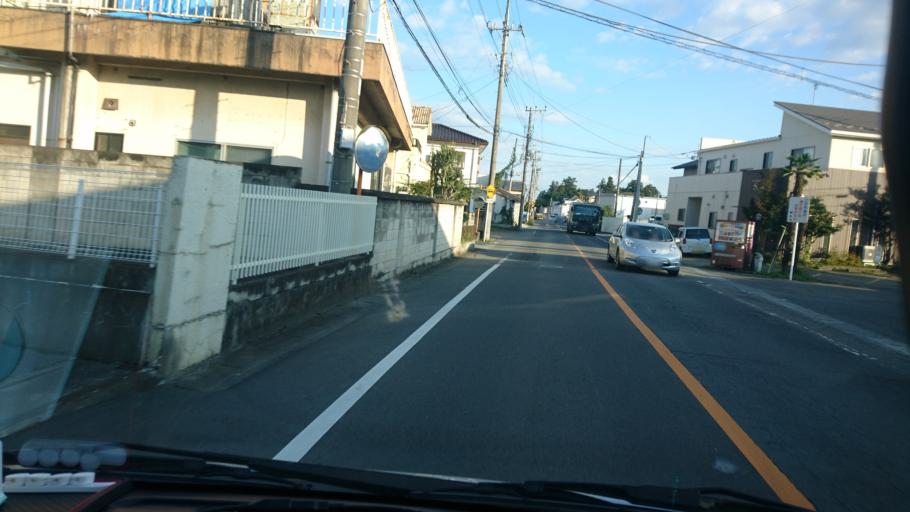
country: JP
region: Gunma
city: Omamacho-omama
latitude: 36.4172
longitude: 139.3014
